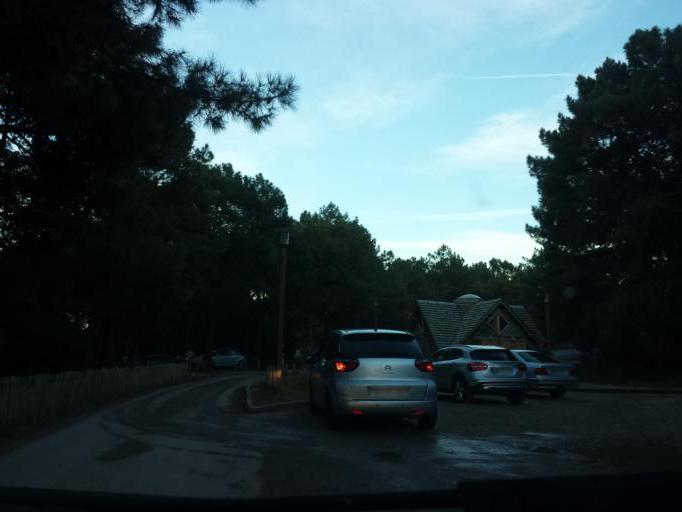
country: FR
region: Aquitaine
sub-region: Departement de la Gironde
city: Arcachon
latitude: 44.5976
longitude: -1.1992
